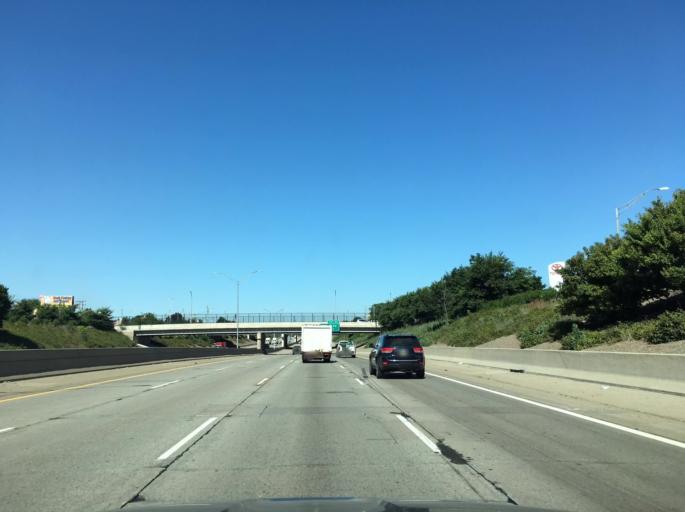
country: US
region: Michigan
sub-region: Macomb County
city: Center Line
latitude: 42.4919
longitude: -83.0246
